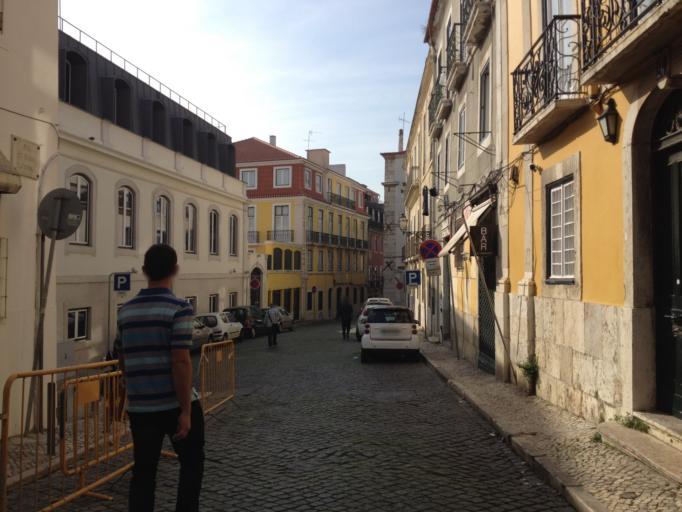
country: PT
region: Lisbon
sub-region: Lisbon
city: Lisbon
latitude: 38.7098
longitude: -9.1487
